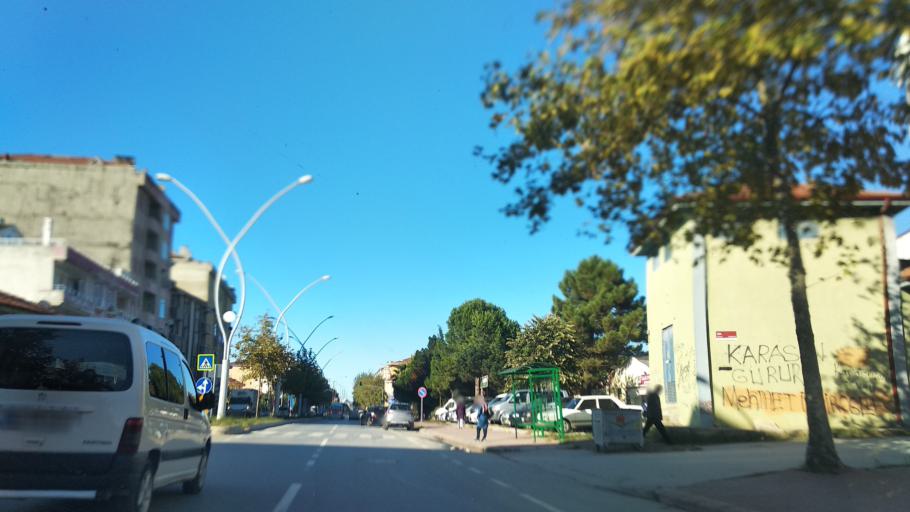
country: TR
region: Sakarya
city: Karasu
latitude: 41.1035
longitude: 30.6926
